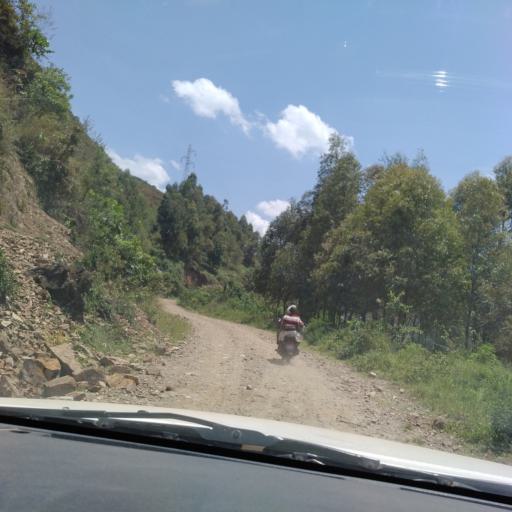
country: CD
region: Nord Kivu
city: Sake
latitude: -1.9742
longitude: 28.9141
